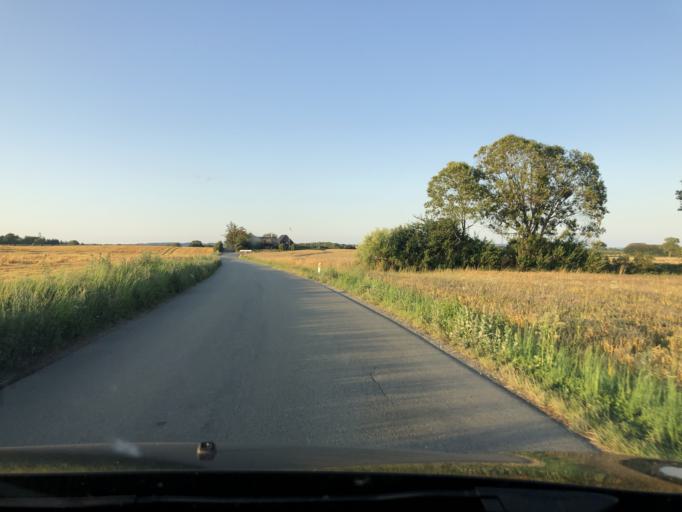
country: DK
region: South Denmark
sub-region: Vejle Kommune
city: Brejning
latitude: 55.6469
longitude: 9.7126
